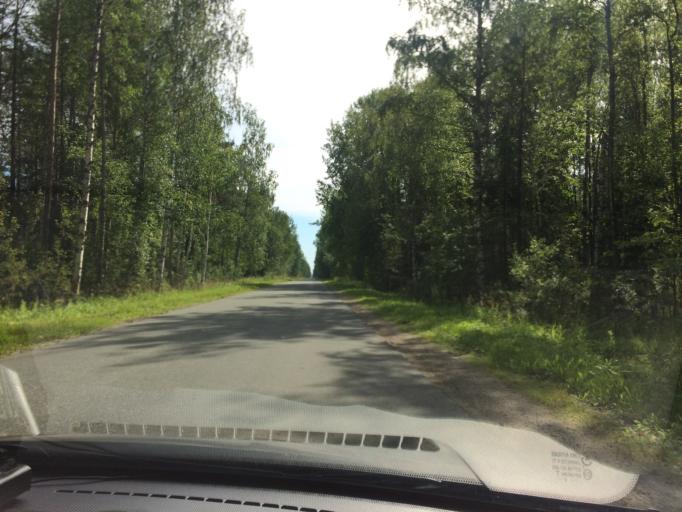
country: RU
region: Mariy-El
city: Surok
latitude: 56.5710
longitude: 48.2164
